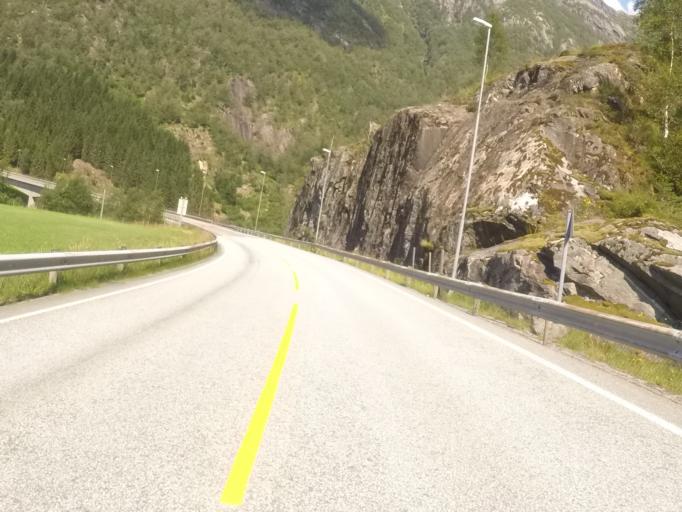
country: NO
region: Hordaland
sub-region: Masfjorden
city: Masfjorden
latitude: 60.9159
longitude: 5.5316
